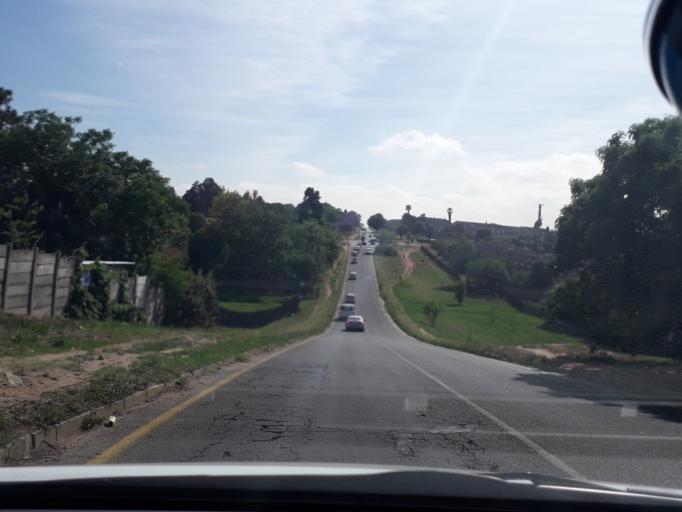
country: ZA
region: Gauteng
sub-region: City of Johannesburg Metropolitan Municipality
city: Roodepoort
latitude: -26.1151
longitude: 27.9439
